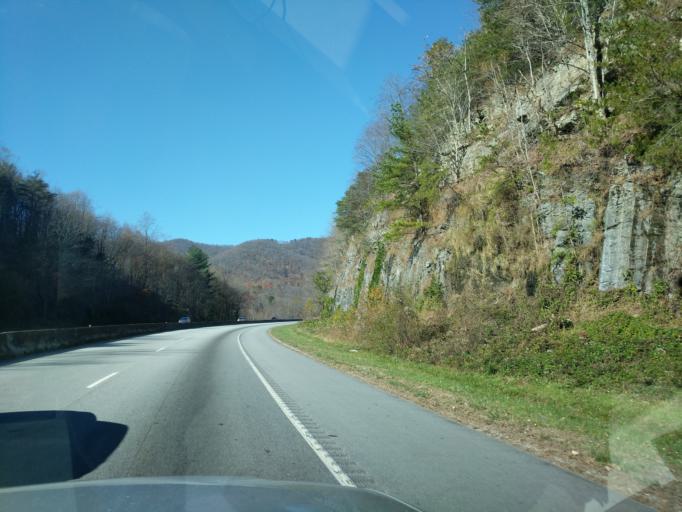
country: US
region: North Carolina
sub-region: Henderson County
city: Flat Rock
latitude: 35.1542
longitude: -82.4712
